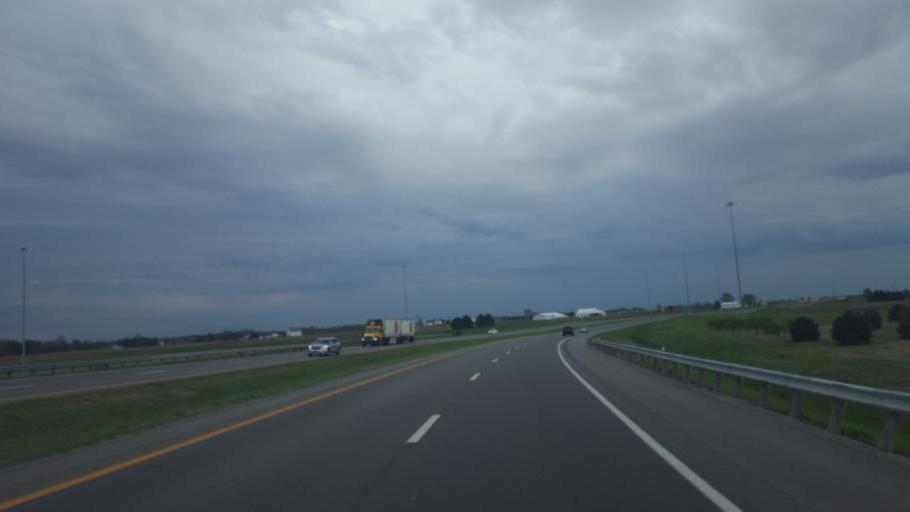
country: US
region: Ohio
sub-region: Wyandot County
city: Upper Sandusky
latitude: 40.8332
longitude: -83.2396
